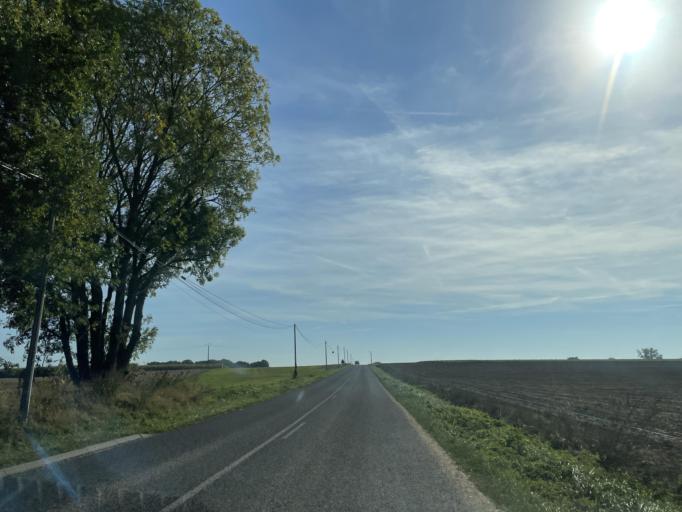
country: FR
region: Ile-de-France
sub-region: Departement de Seine-et-Marne
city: Saint-Jean-les-Deux-Jumeaux
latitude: 48.9071
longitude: 3.0246
